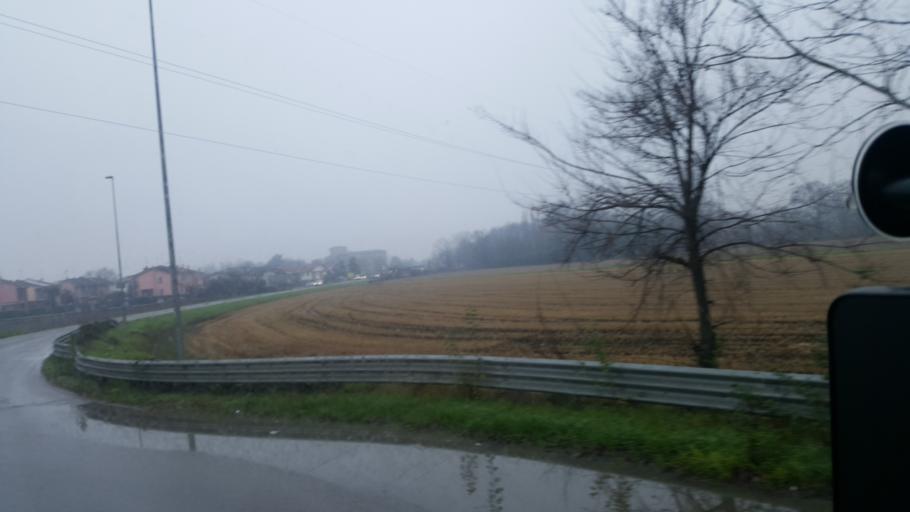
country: IT
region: Lombardy
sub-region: Provincia di Pavia
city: Lardirago
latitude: 45.2409
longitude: 9.2332
